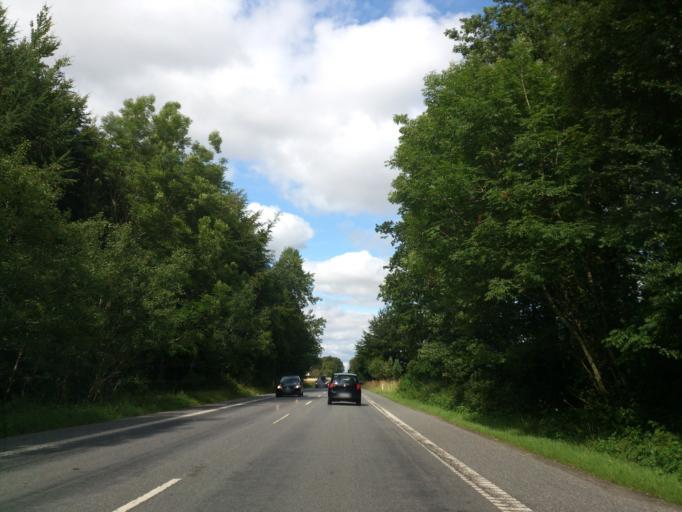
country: DK
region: South Denmark
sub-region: Aabenraa Kommune
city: Krusa
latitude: 54.8841
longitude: 9.4192
